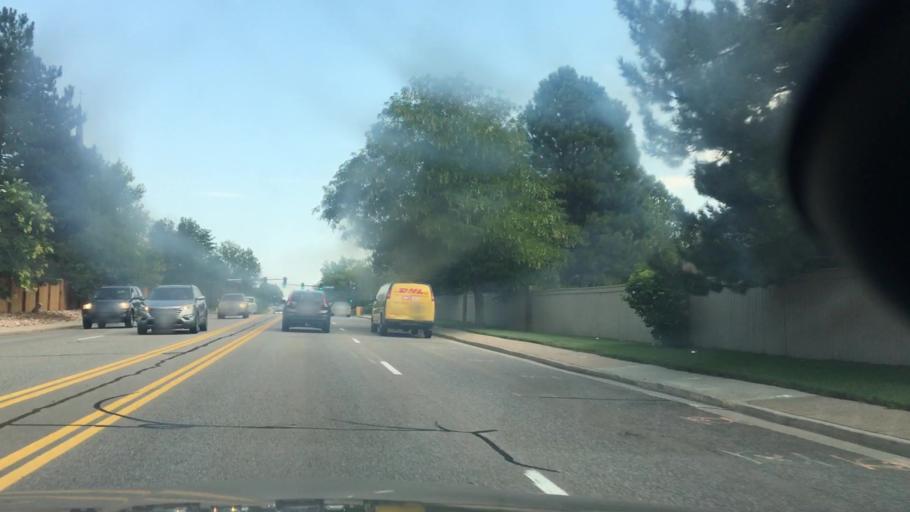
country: US
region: Colorado
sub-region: Arapahoe County
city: Castlewood
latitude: 39.5806
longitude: -104.8912
